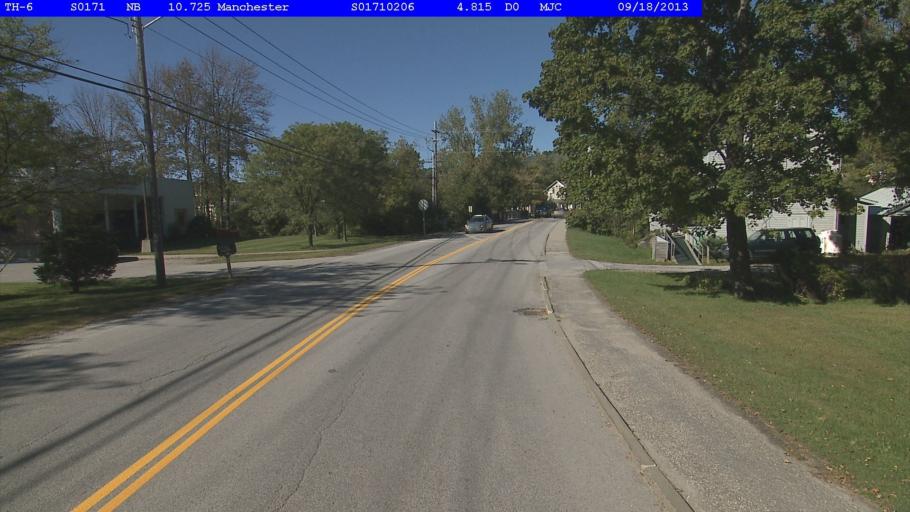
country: US
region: Vermont
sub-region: Bennington County
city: Manchester Center
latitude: 43.1720
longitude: -73.0488
